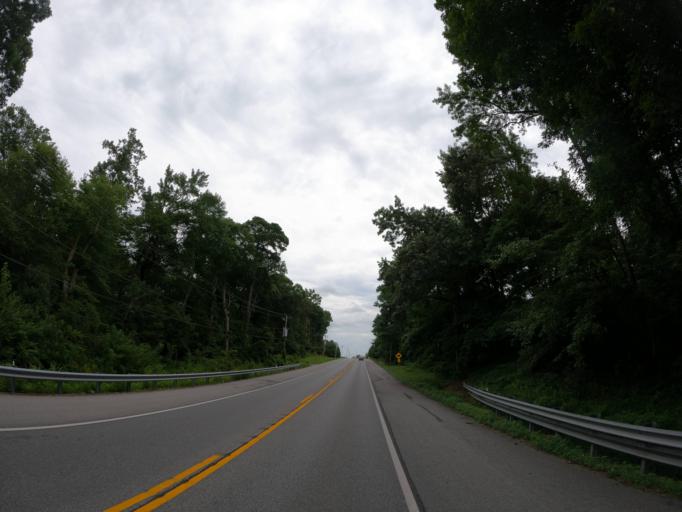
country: US
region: Maryland
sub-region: Saint Mary's County
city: California
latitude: 38.2383
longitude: -76.5333
